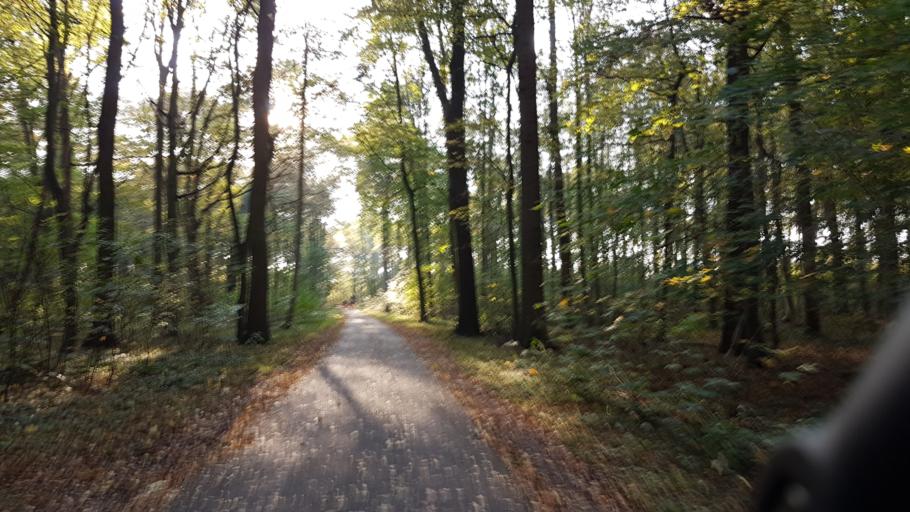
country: DE
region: Lower Saxony
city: Hannover
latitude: 52.3706
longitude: 9.7821
